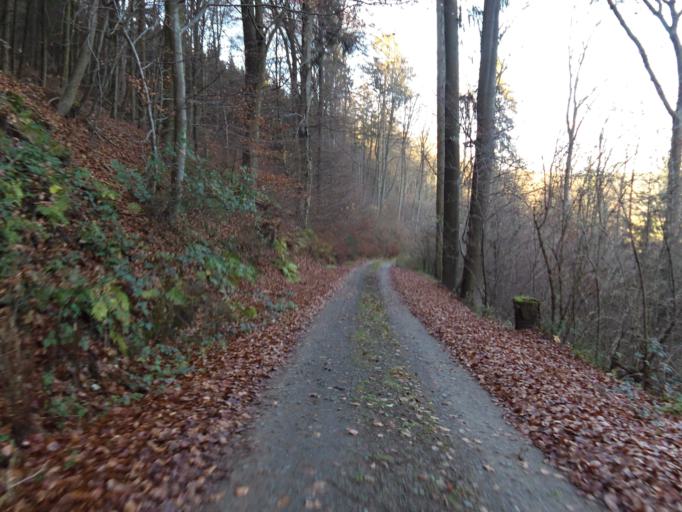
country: DE
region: Rheinland-Pfalz
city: Altleiningen
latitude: 49.4792
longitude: 8.0906
